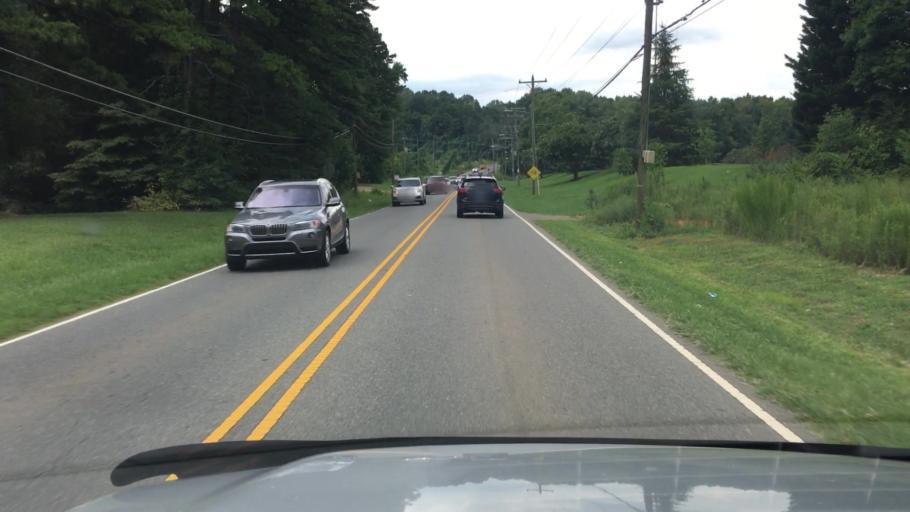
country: US
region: North Carolina
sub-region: Mecklenburg County
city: Huntersville
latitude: 35.3221
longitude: -80.8657
